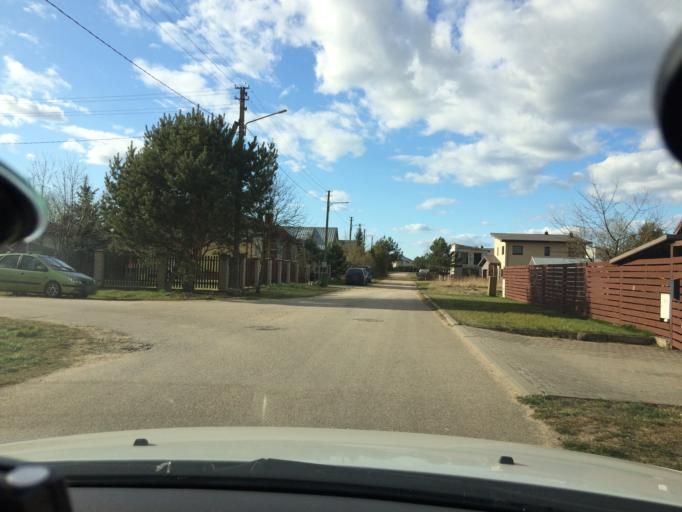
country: LT
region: Vilnius County
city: Rasos
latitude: 54.7758
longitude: 25.3523
